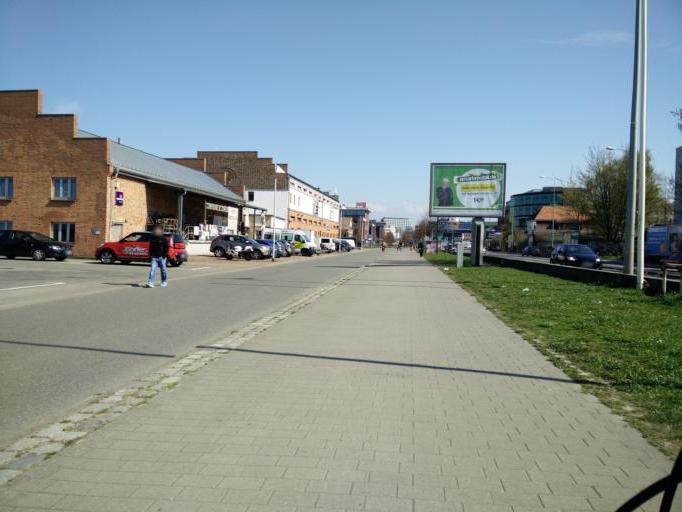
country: DE
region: Mecklenburg-Vorpommern
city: Rostock
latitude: 54.0938
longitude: 12.1158
